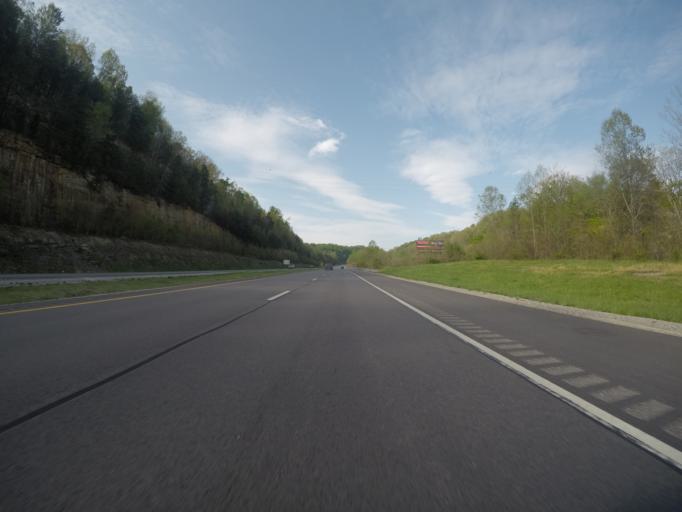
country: US
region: West Virginia
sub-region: Kanawha County
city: Dunbar
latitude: 38.3071
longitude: -81.7336
